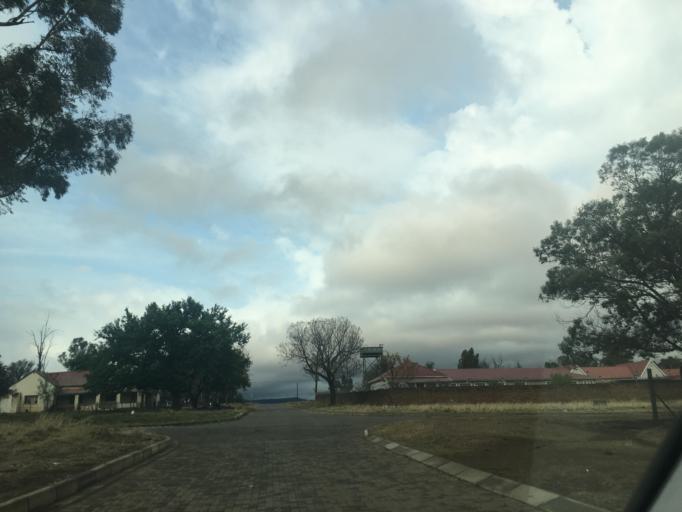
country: ZA
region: Eastern Cape
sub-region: Chris Hani District Municipality
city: Cala
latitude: -31.5251
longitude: 27.7006
